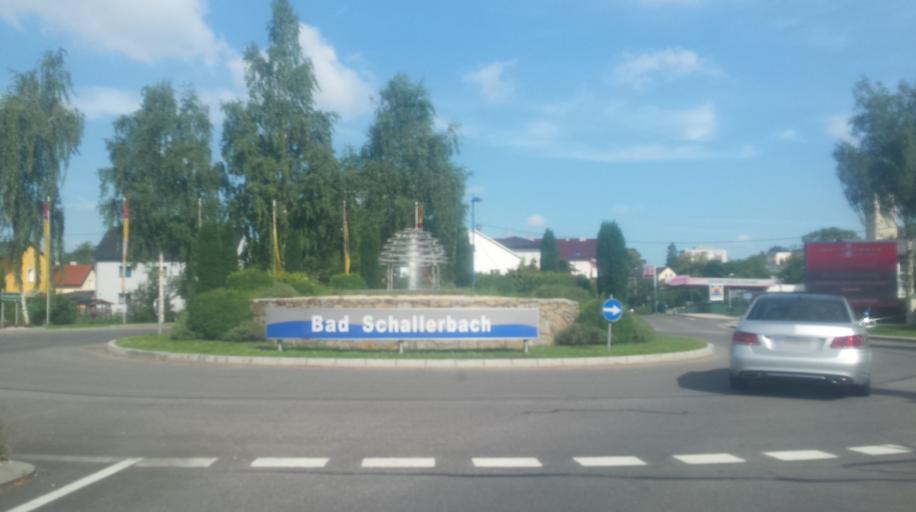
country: AT
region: Upper Austria
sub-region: Politischer Bezirk Grieskirchen
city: Bad Schallerbach
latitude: 48.2265
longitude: 13.9263
